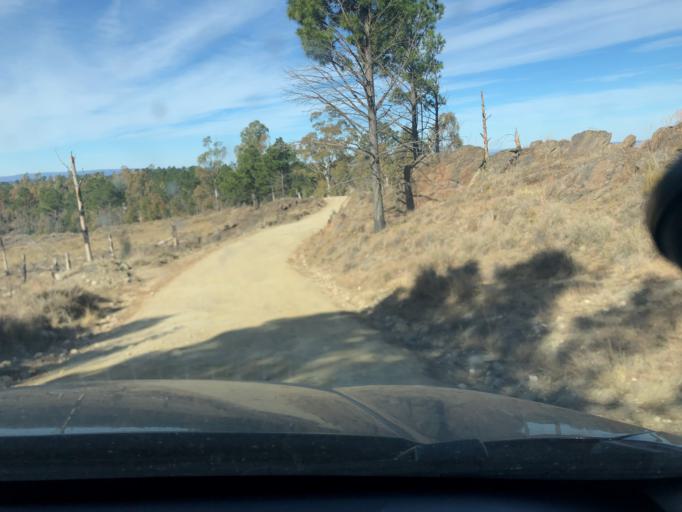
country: AR
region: Cordoba
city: Villa Berna
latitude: -31.9635
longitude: -64.8079
